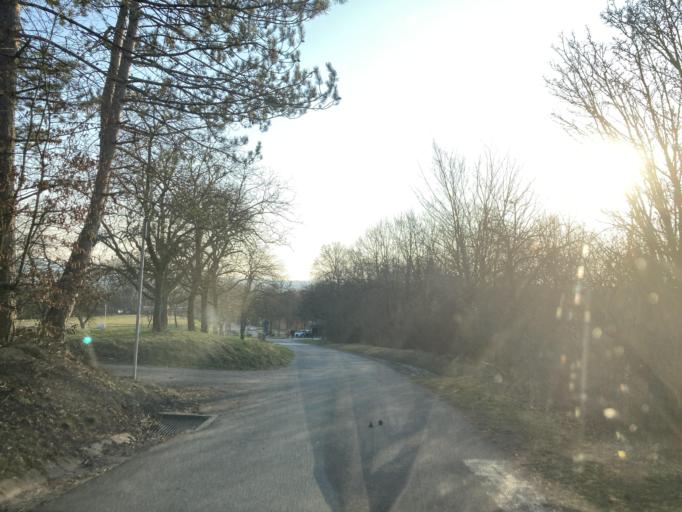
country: DE
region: Baden-Wuerttemberg
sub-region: Tuebingen Region
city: Rottenburg
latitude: 48.5042
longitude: 8.9719
